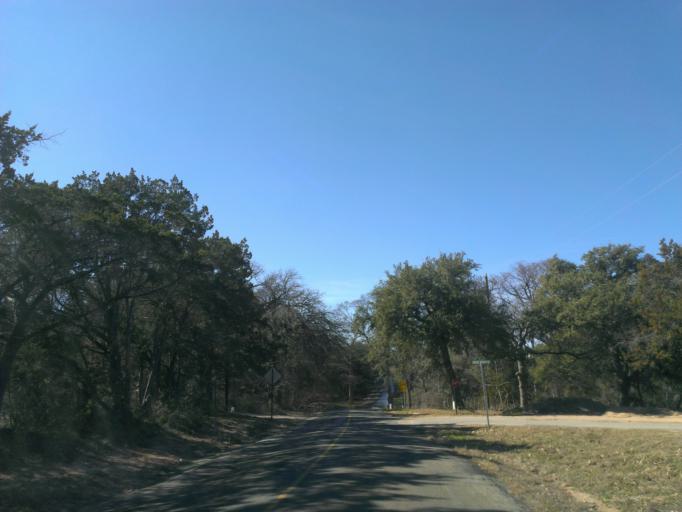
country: US
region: Texas
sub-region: Travis County
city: Briarcliff
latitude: 30.4769
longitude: -98.1519
